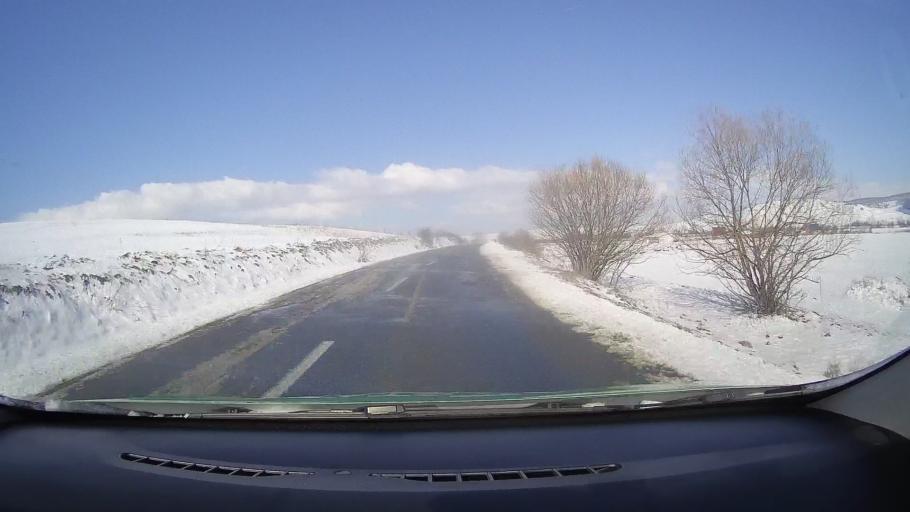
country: RO
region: Sibiu
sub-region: Comuna Rosia
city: Rosia
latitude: 45.8296
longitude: 24.3126
